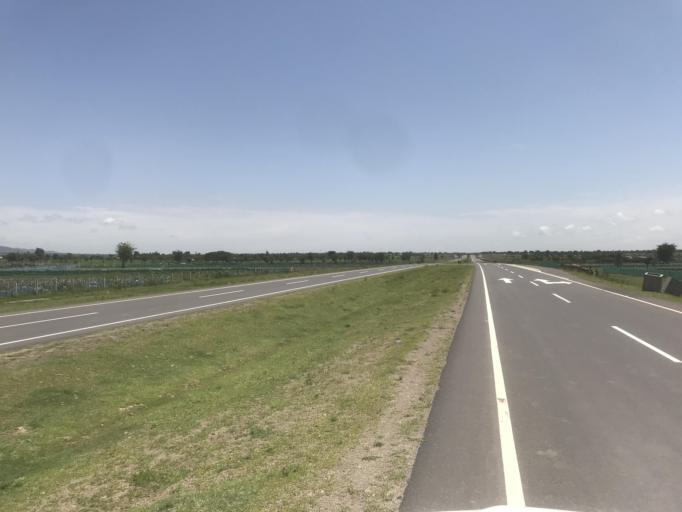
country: ET
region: Oromiya
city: Mojo
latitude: 8.3343
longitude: 38.9658
